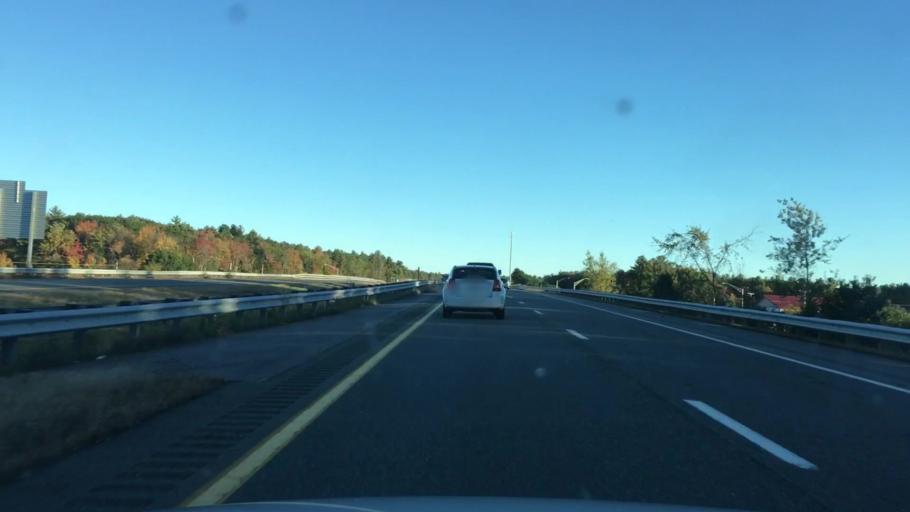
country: US
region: New Hampshire
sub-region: Rockingham County
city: Exeter
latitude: 42.9939
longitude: -70.9284
